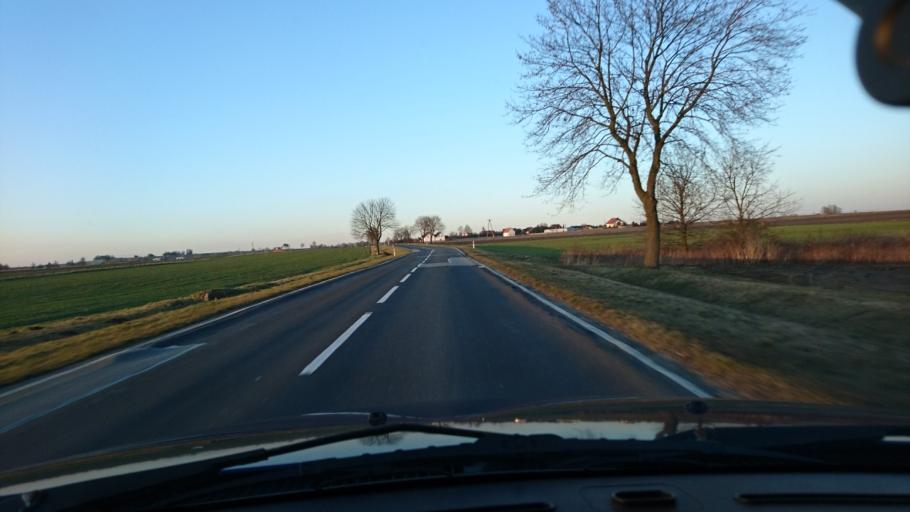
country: PL
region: Silesian Voivodeship
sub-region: Powiat gliwicki
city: Wielowies
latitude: 50.4647
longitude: 18.6110
